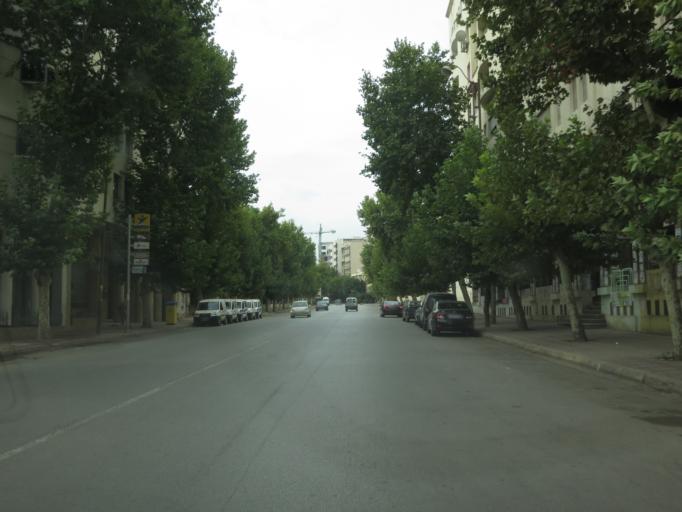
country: MA
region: Fes-Boulemane
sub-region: Fes
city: Fes
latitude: 34.0419
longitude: -5.0036
